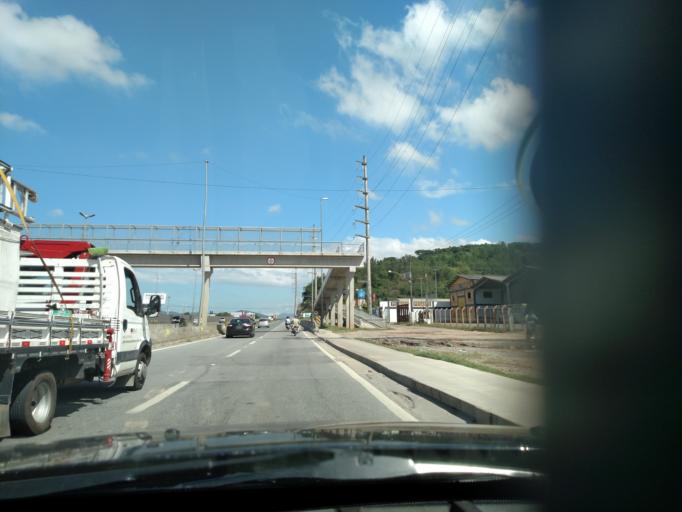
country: BR
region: Santa Catarina
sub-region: Itajai
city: Itajai
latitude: -26.8935
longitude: -48.7202
